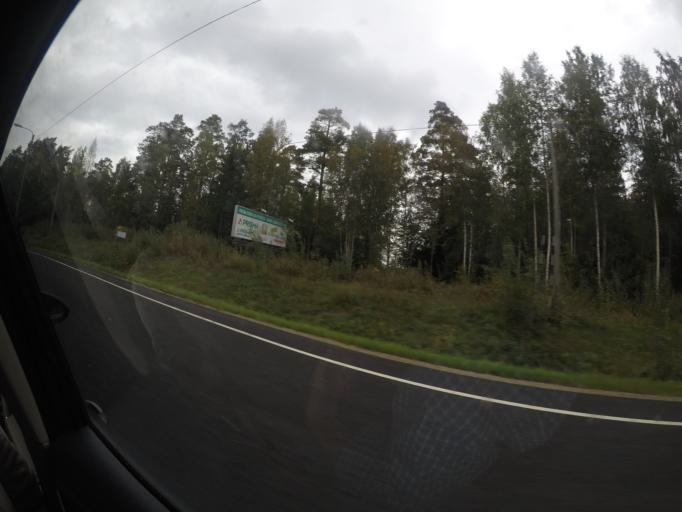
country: FI
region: Pirkanmaa
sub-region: Tampere
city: Kangasala
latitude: 61.4464
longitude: 24.1085
